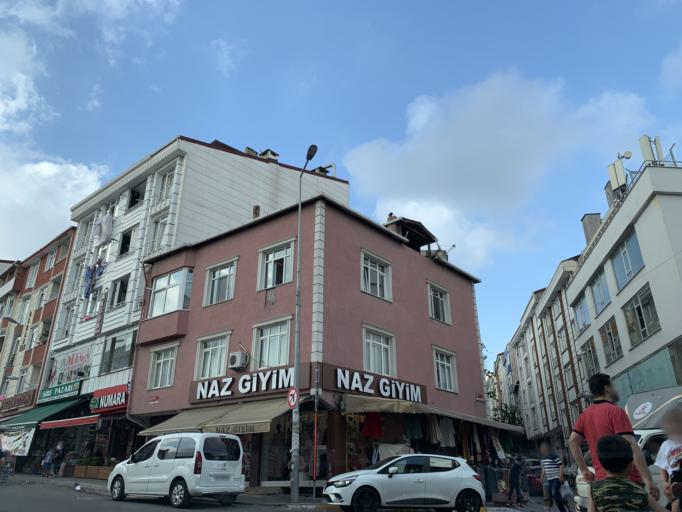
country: TR
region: Istanbul
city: Esenyurt
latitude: 41.0247
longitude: 28.6754
